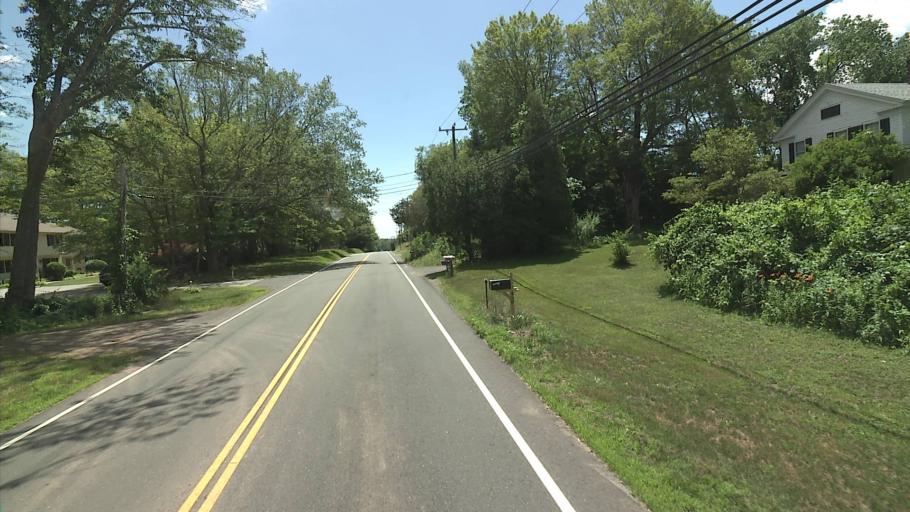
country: US
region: Connecticut
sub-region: Middlesex County
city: East Haddam
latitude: 41.4750
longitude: -72.4449
